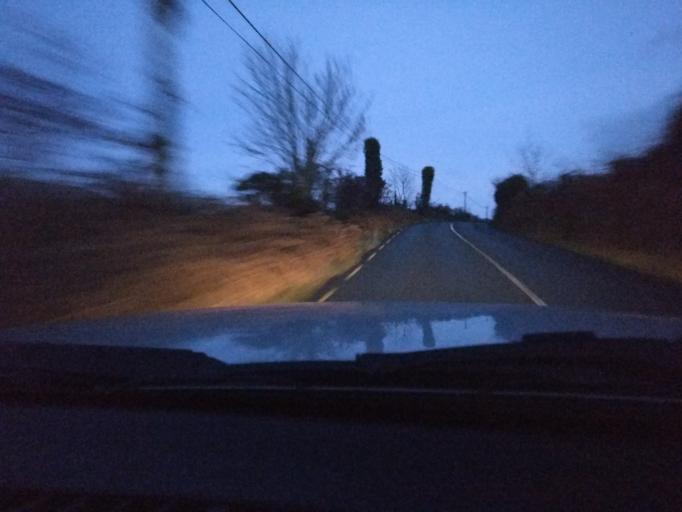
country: GB
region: Northern Ireland
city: Rostrevor
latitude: 54.0684
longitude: -6.2254
